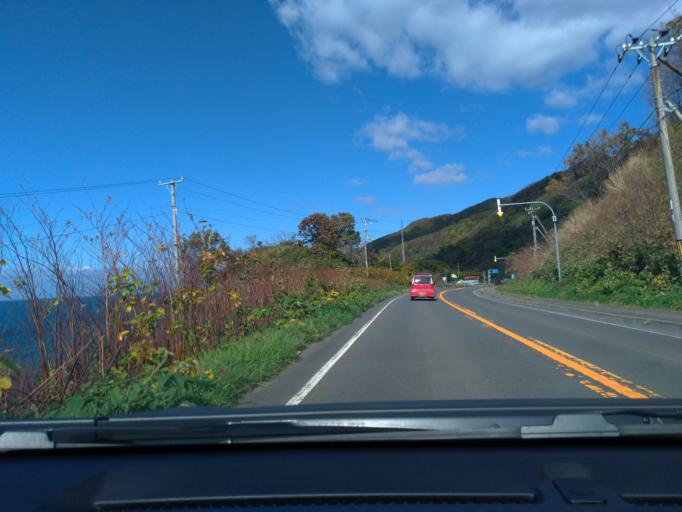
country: JP
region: Hokkaido
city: Ishikari
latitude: 43.4177
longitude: 141.4296
